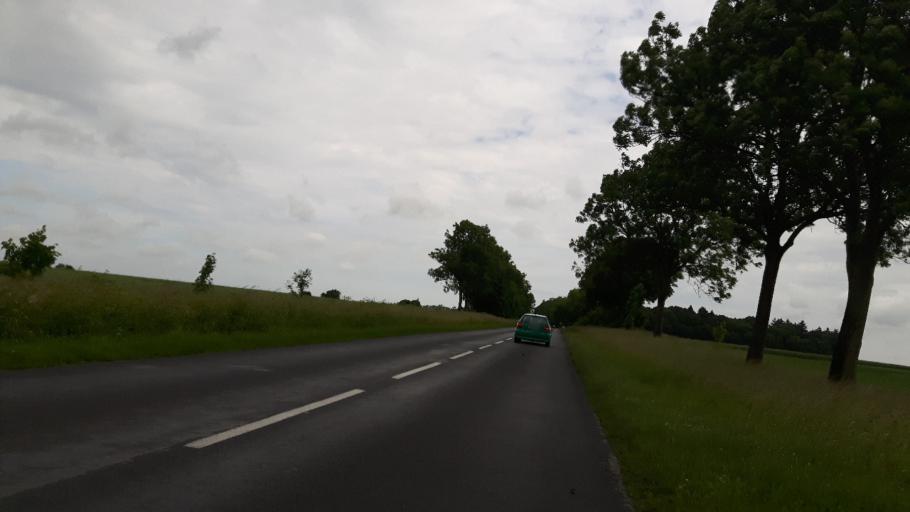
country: PL
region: West Pomeranian Voivodeship
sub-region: Powiat gryficki
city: Gryfice
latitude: 53.9513
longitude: 15.2259
